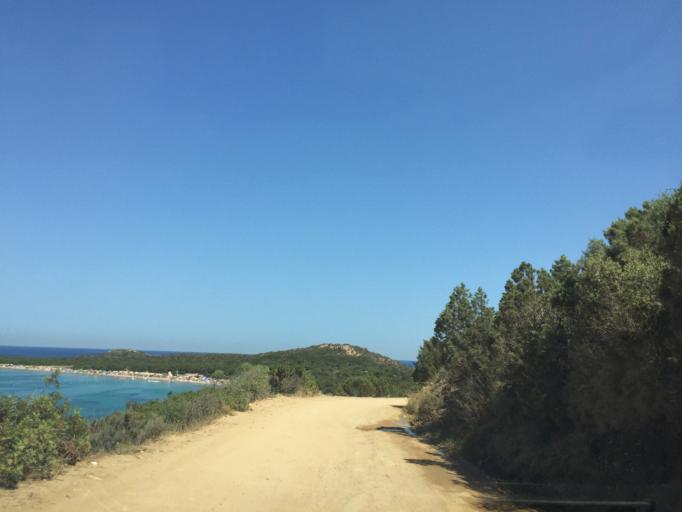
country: IT
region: Sardinia
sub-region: Provincia di Olbia-Tempio
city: San Teodoro
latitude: 40.8406
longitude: 9.7176
